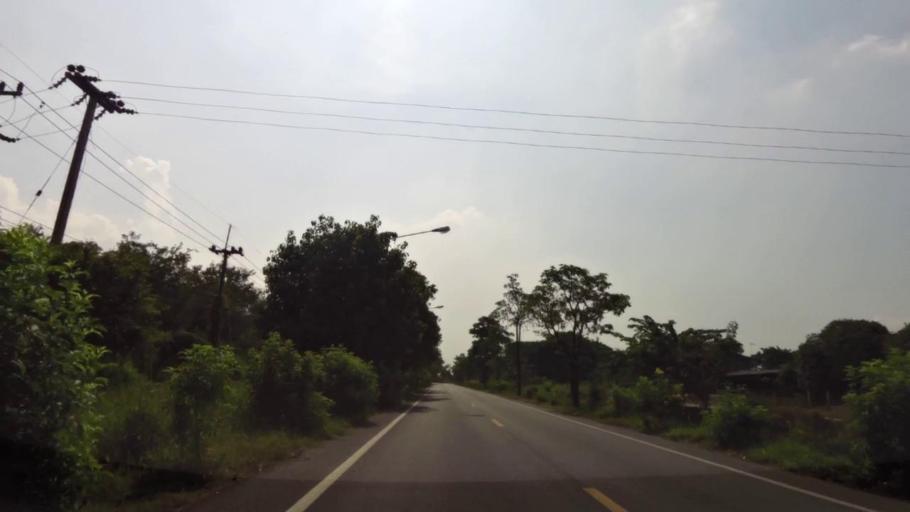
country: TH
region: Ang Thong
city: Wiset Chaichan
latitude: 14.6015
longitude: 100.3954
